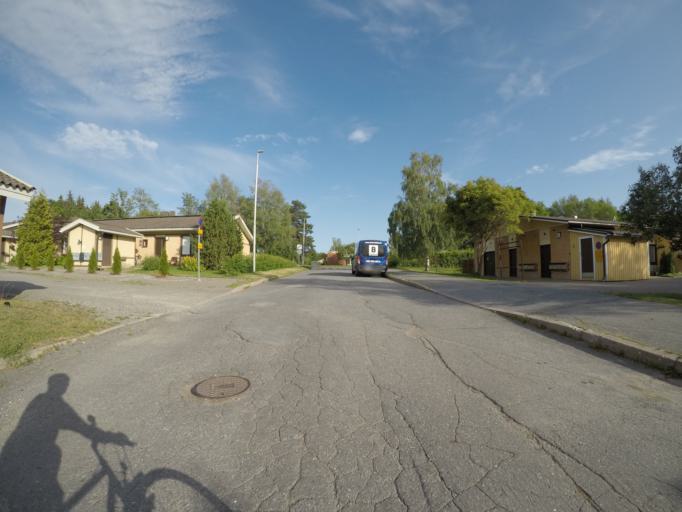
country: FI
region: Haeme
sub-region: Haemeenlinna
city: Haemeenlinna
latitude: 60.9777
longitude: 24.4000
